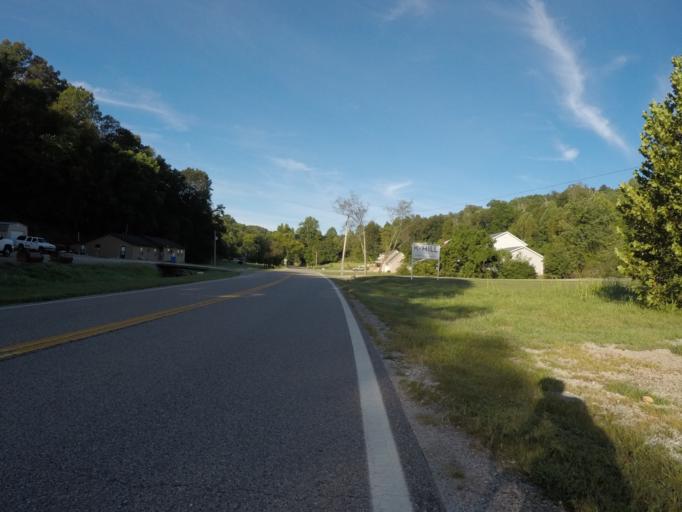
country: US
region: Ohio
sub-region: Lawrence County
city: Coal Grove
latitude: 38.5737
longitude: -82.5459
